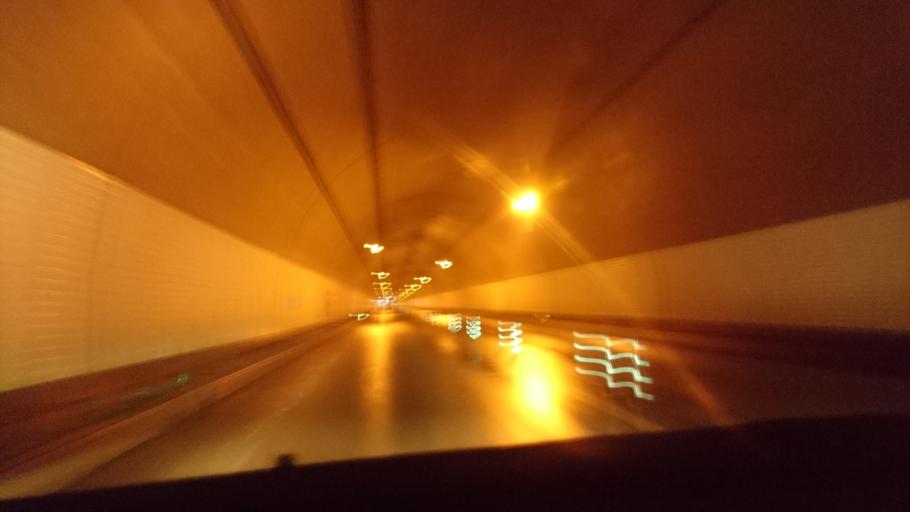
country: JP
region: Iwate
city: Miyako
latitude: 39.8545
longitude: 141.9439
